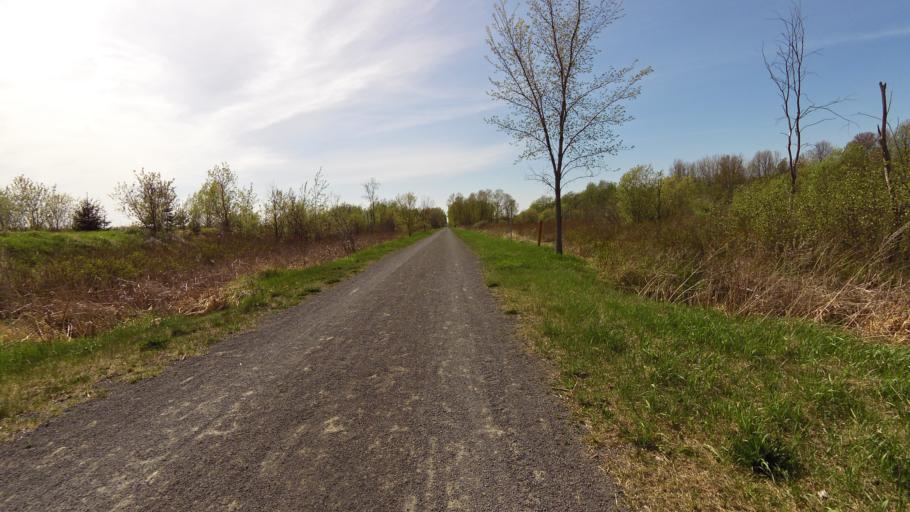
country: CA
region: Ontario
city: Clarence-Rockland
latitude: 45.4185
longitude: -75.4704
